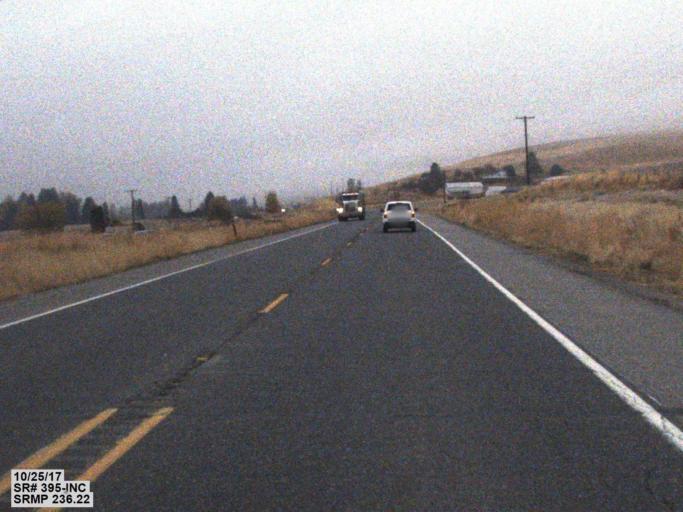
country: US
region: Washington
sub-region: Stevens County
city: Kettle Falls
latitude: 48.6013
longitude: -118.0177
